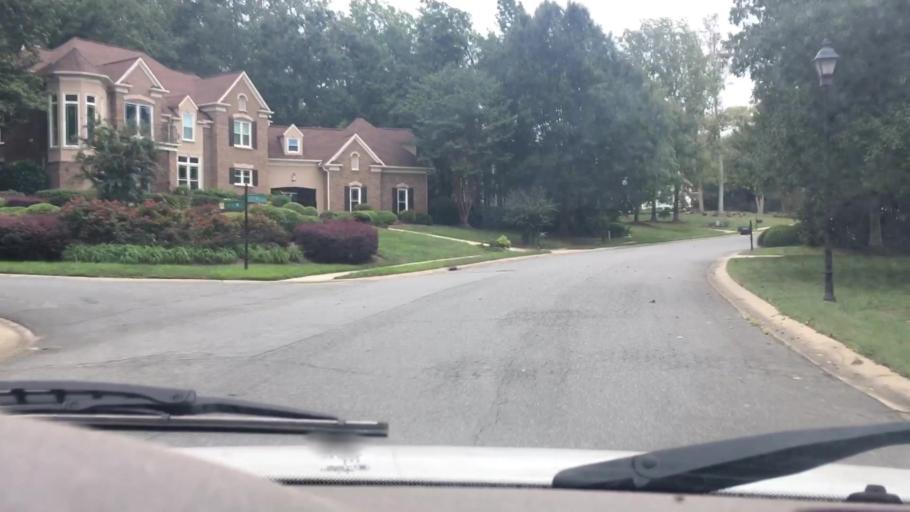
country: US
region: North Carolina
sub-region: Gaston County
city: Davidson
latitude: 35.4661
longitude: -80.8062
